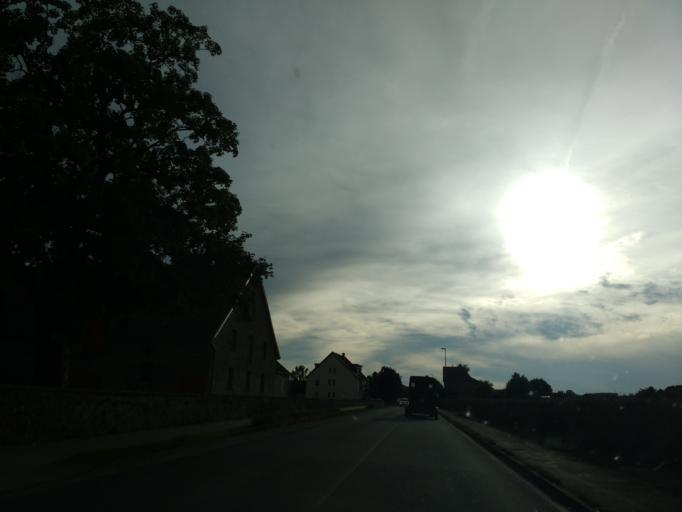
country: DE
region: North Rhine-Westphalia
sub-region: Regierungsbezirk Detmold
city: Blomberg
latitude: 51.9420
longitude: 9.0294
